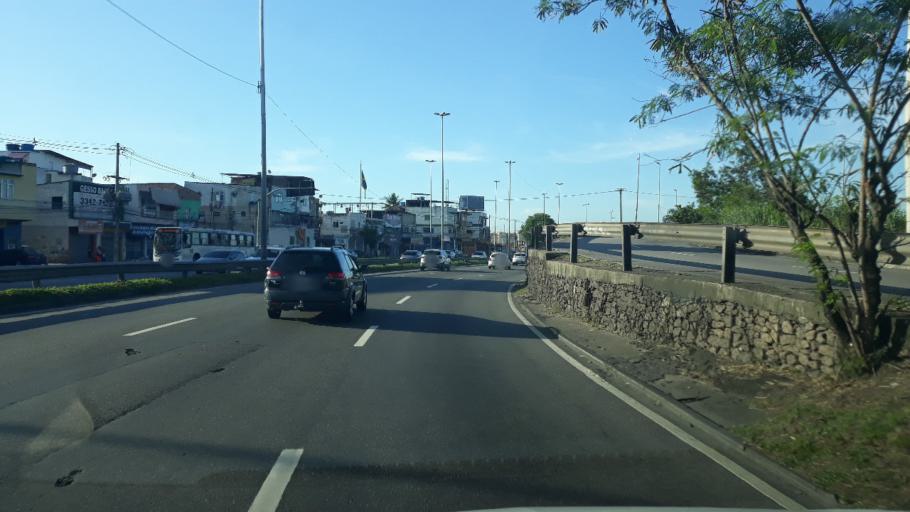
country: BR
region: Rio de Janeiro
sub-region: Sao Joao De Meriti
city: Sao Joao de Meriti
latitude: -22.9566
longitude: -43.3567
